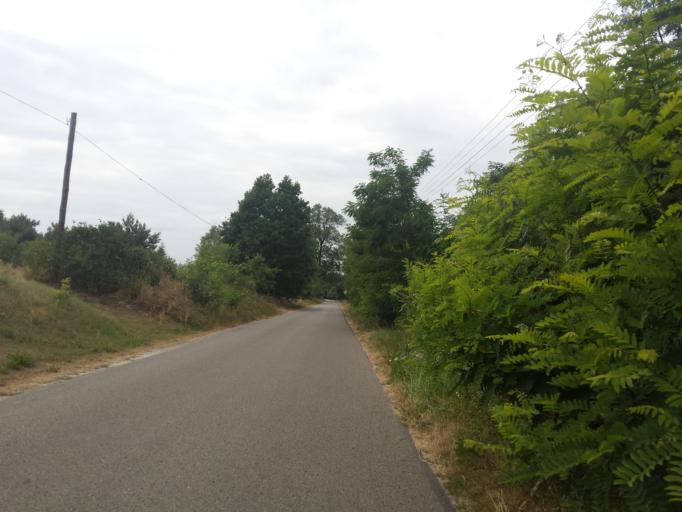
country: PL
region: Swietokrzyskie
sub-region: Powiat staszowski
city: Bogoria
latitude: 50.6585
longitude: 21.2061
